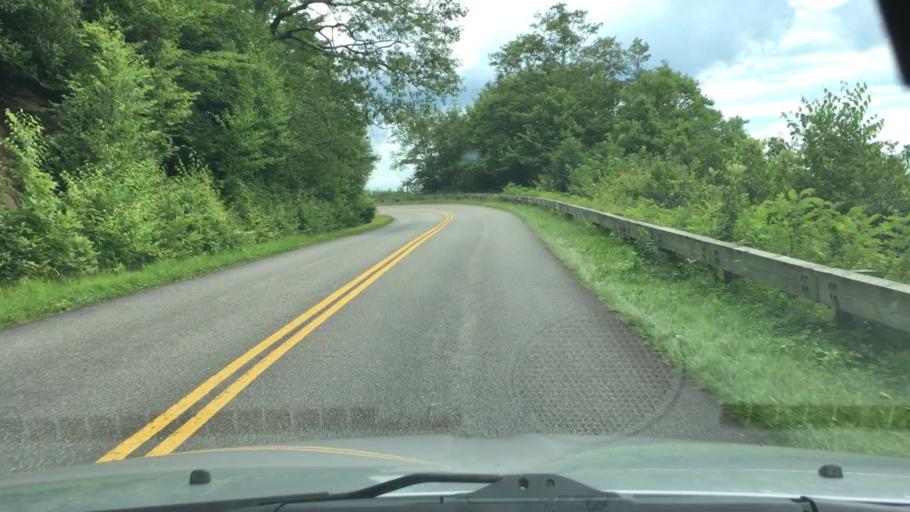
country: US
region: North Carolina
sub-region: Buncombe County
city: Black Mountain
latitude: 35.7119
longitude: -82.2381
